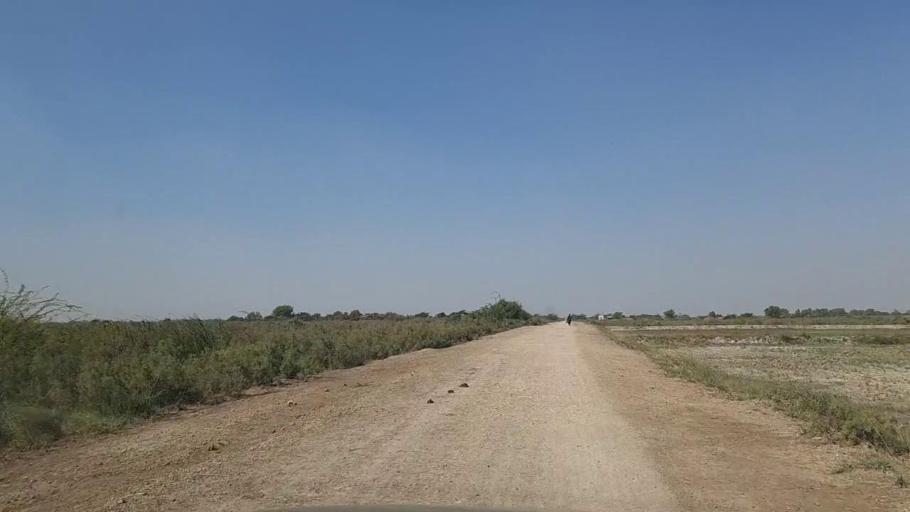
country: PK
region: Sindh
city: Daro Mehar
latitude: 24.8301
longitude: 68.1456
